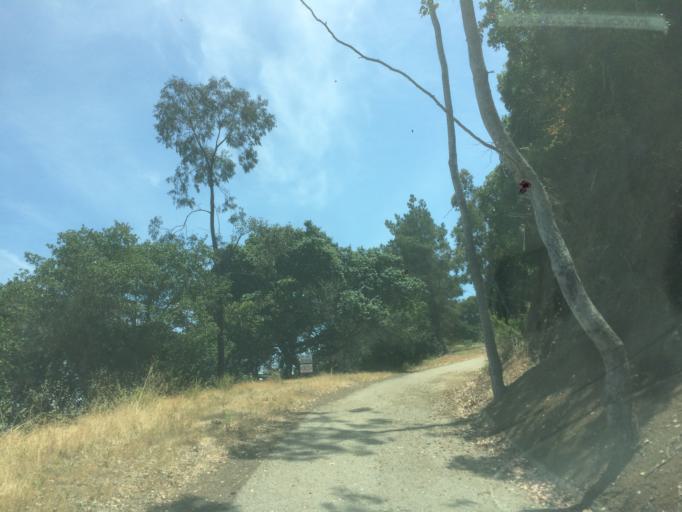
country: US
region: California
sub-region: San Luis Obispo County
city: San Luis Obispo
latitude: 35.2557
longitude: -120.7003
